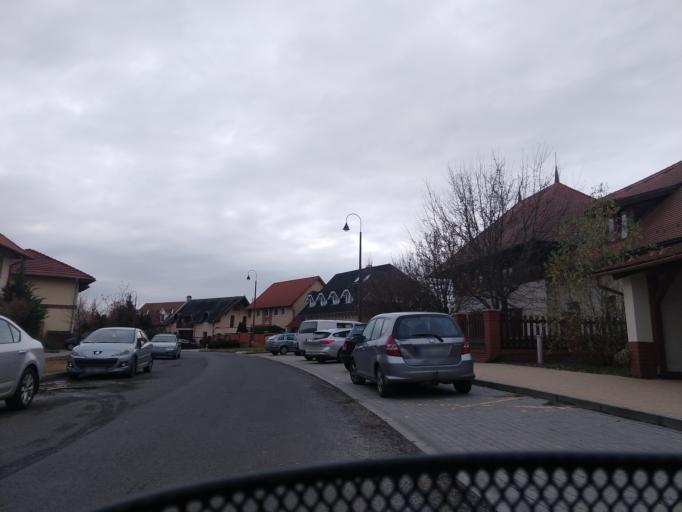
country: HU
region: Pest
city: Veresegyhaz
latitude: 47.6522
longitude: 19.2641
